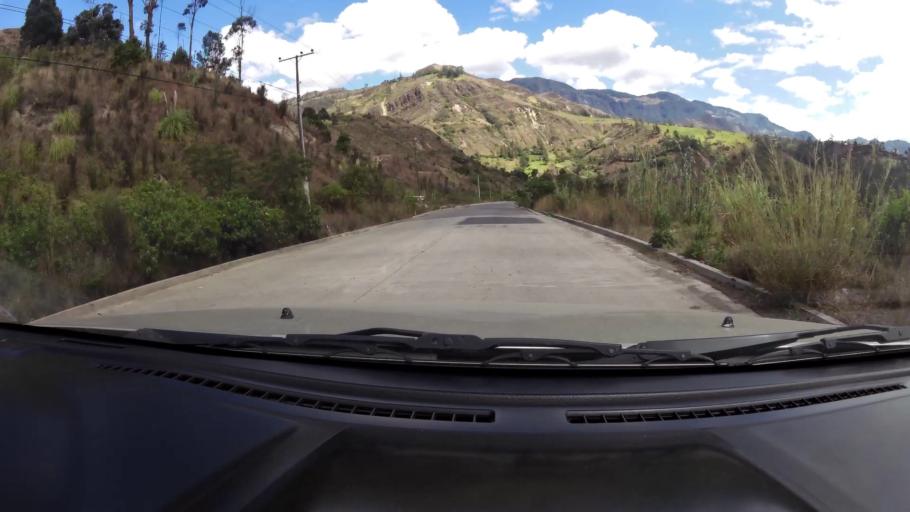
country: EC
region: Azuay
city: Cuenca
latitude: -3.1731
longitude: -79.1618
